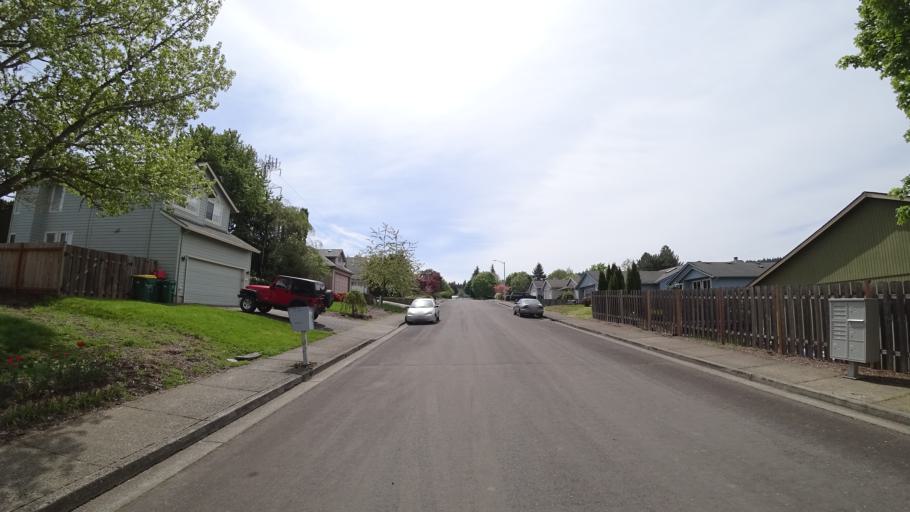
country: US
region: Oregon
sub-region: Washington County
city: Aloha
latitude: 45.4611
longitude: -122.8420
